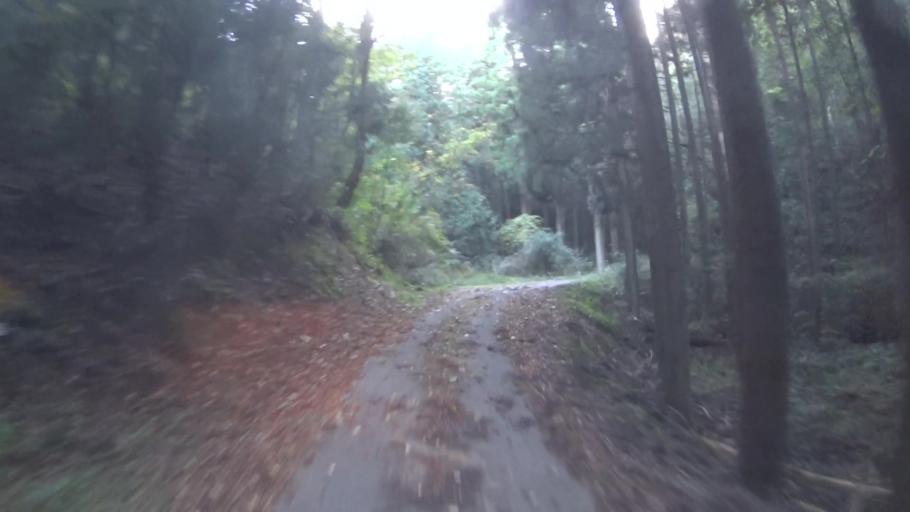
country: JP
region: Kyoto
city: Ayabe
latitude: 35.2702
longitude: 135.2488
